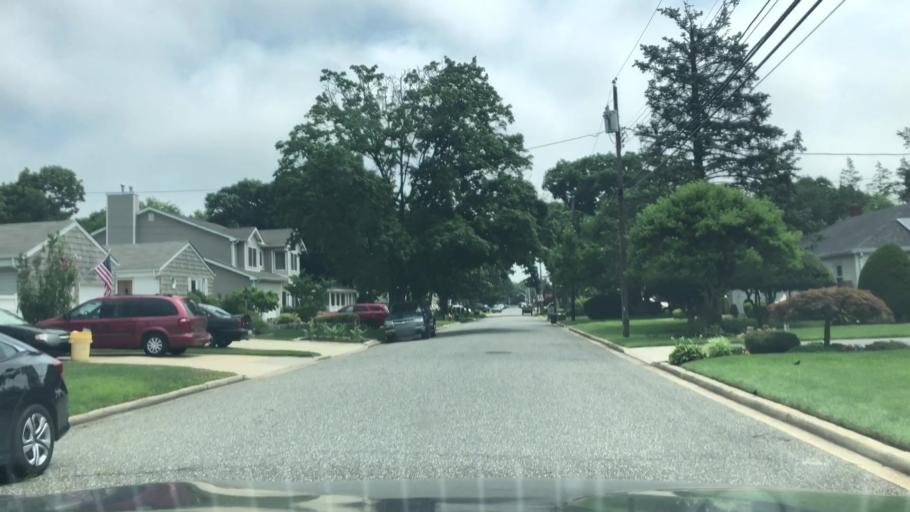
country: US
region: New York
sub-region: Nassau County
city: North Massapequa
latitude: 40.7047
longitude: -73.4663
